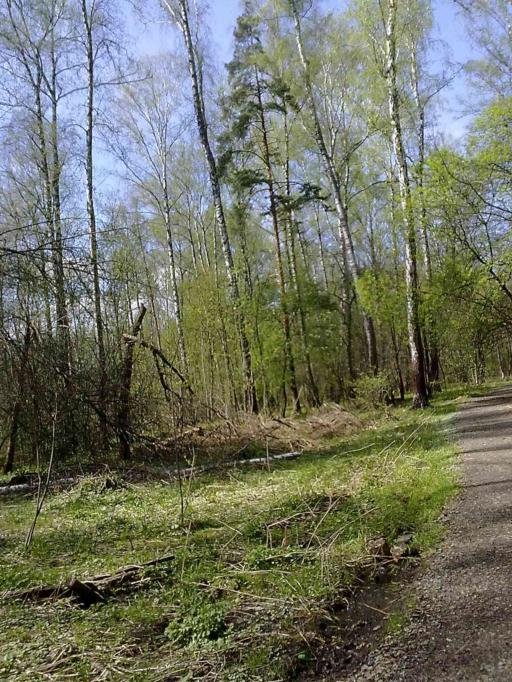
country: RU
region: Moscow
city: Novo-Peredelkino
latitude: 55.6475
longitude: 37.3114
